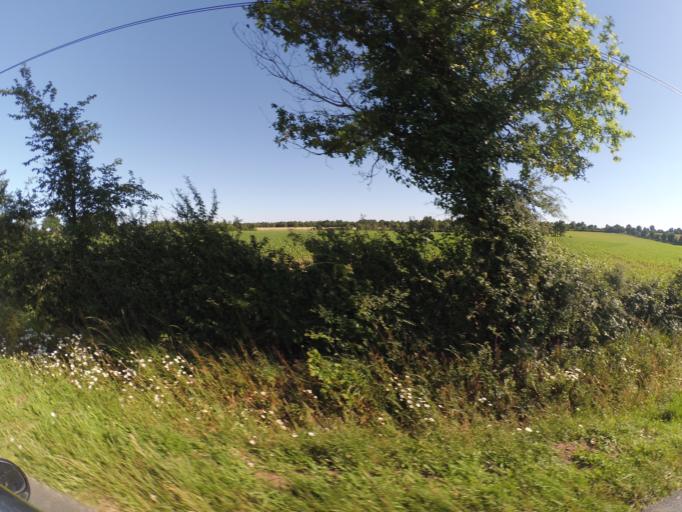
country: FR
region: Pays de la Loire
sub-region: Departement de la Vendee
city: Beaurepaire
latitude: 46.9072
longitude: -1.1148
